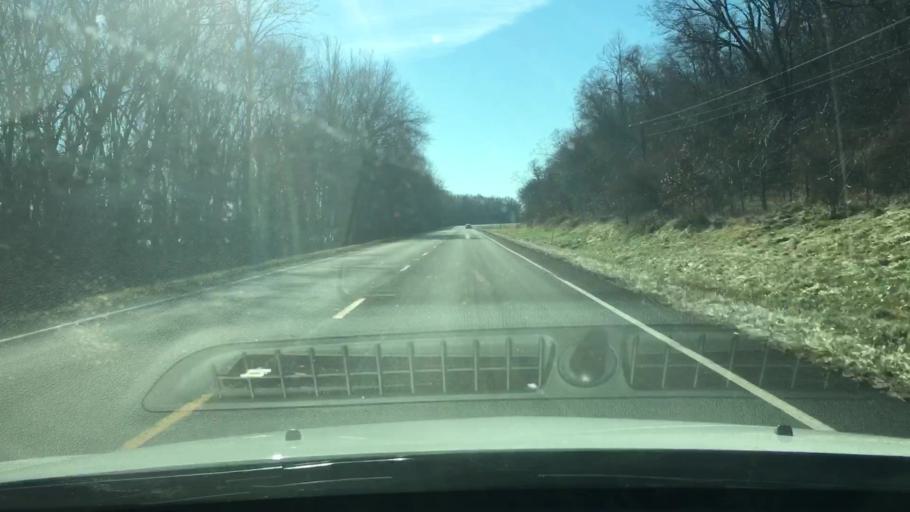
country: US
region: Illinois
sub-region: Fulton County
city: Canton
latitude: 40.4519
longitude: -89.9619
